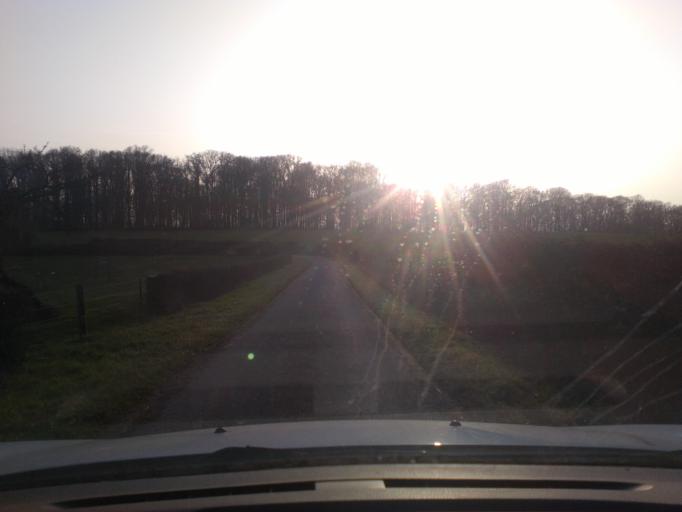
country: FR
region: Lorraine
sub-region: Departement des Vosges
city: Vittel
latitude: 48.2591
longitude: 6.0004
